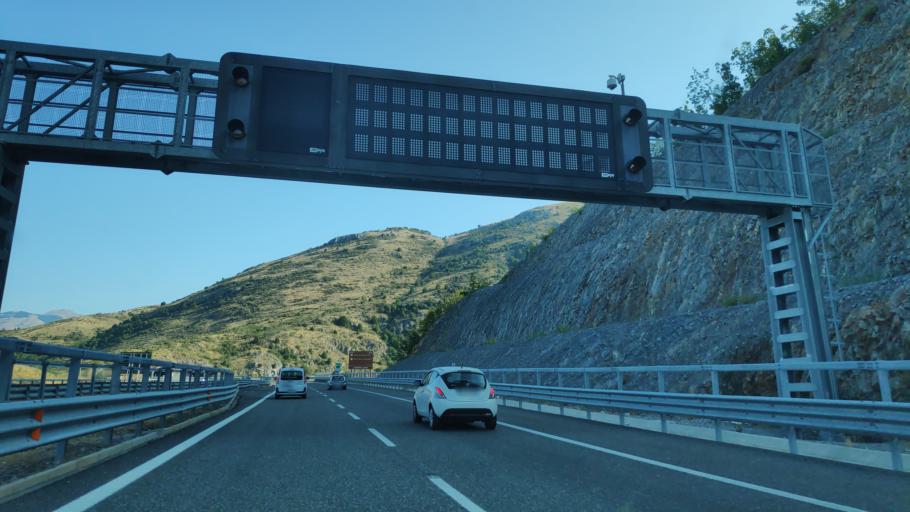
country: IT
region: Basilicate
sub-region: Provincia di Potenza
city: Lauria
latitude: 40.0328
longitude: 15.8746
